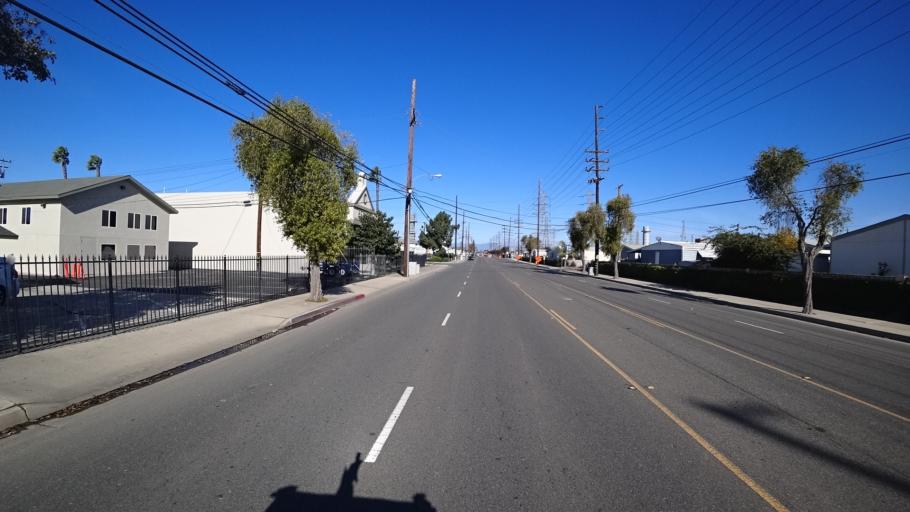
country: US
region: California
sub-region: Orange County
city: Stanton
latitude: 33.8050
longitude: -117.9846
